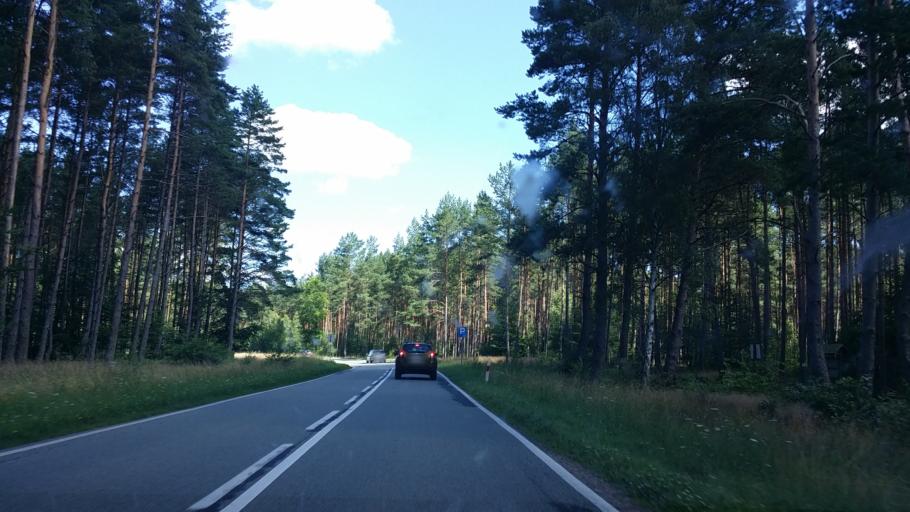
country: PL
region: West Pomeranian Voivodeship
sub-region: Powiat drawski
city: Drawsko Pomorskie
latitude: 53.4300
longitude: 15.8269
